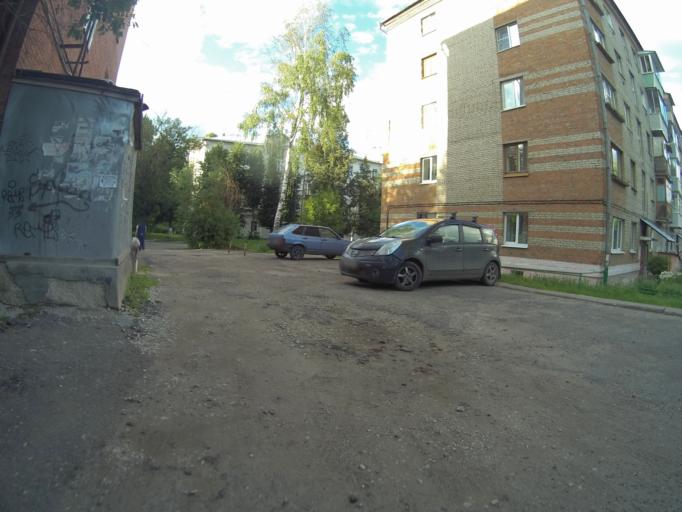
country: RU
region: Vladimir
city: Vladimir
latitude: 56.1488
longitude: 40.4236
